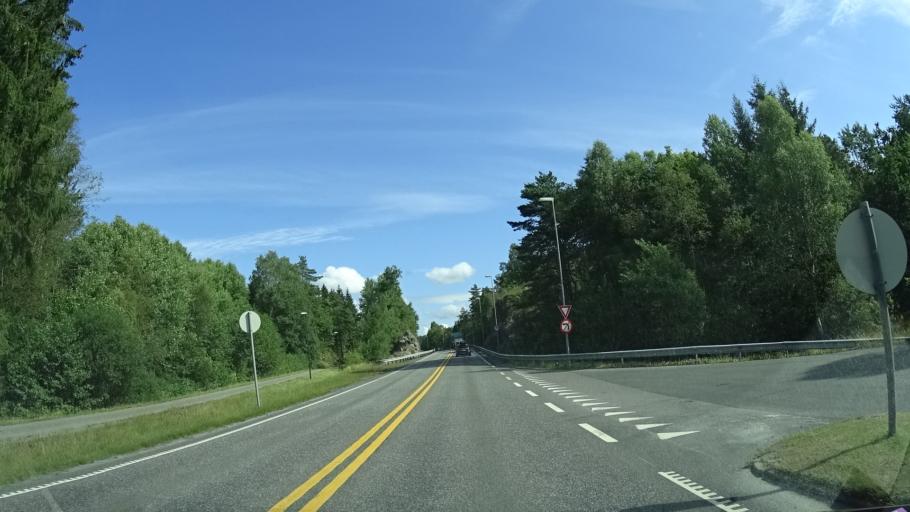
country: NO
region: Telemark
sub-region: Bamble
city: Langesund
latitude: 59.0243
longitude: 9.6786
